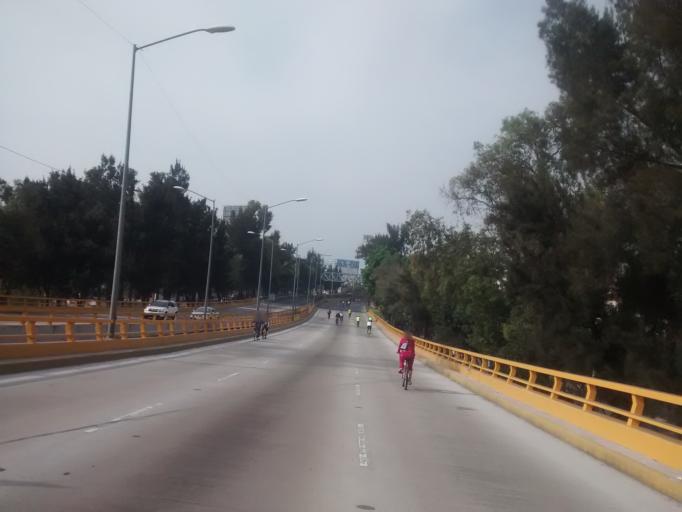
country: MX
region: Mexico City
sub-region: Iztacalco
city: Iztacalco
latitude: 19.3715
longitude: -99.1038
